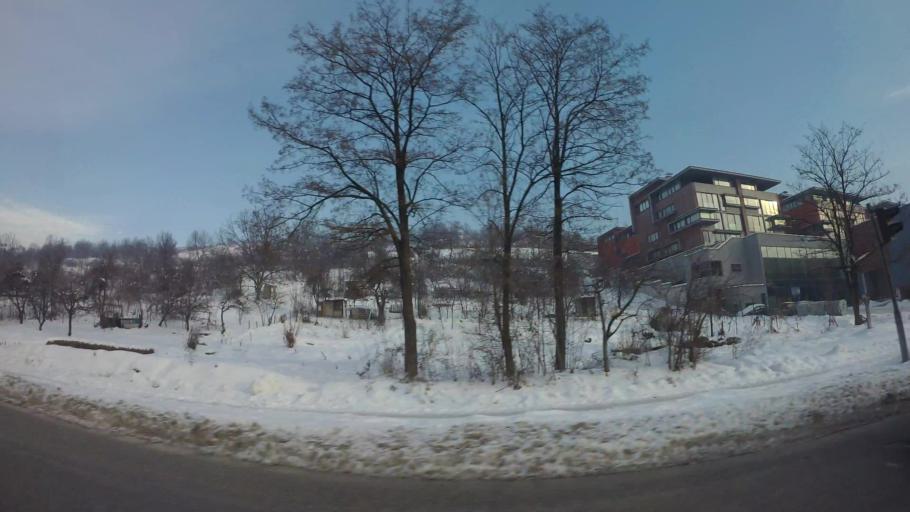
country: BA
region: Federation of Bosnia and Herzegovina
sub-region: Kanton Sarajevo
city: Sarajevo
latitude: 43.8318
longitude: 18.3515
